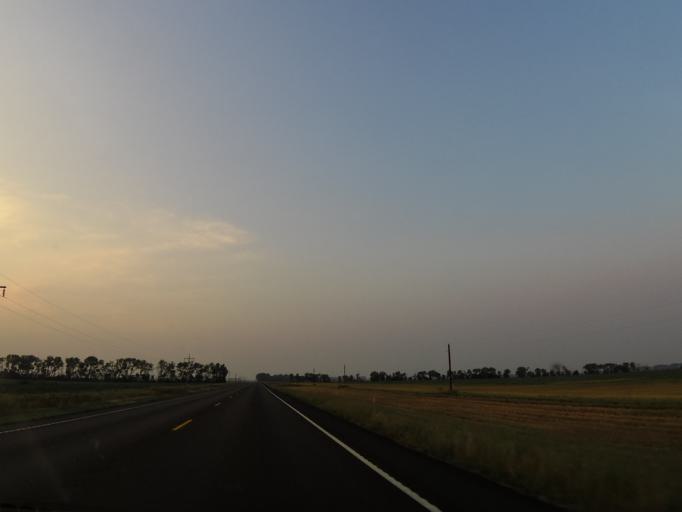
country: US
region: North Dakota
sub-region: Walsh County
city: Park River
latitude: 48.3565
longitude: -97.6223
